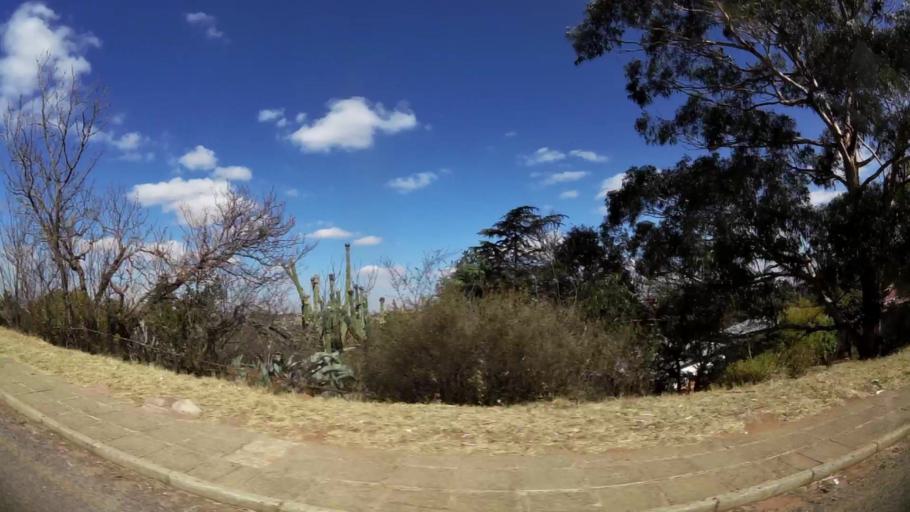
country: ZA
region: Gauteng
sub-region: West Rand District Municipality
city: Krugersdorp
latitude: -26.0967
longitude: 27.7829
